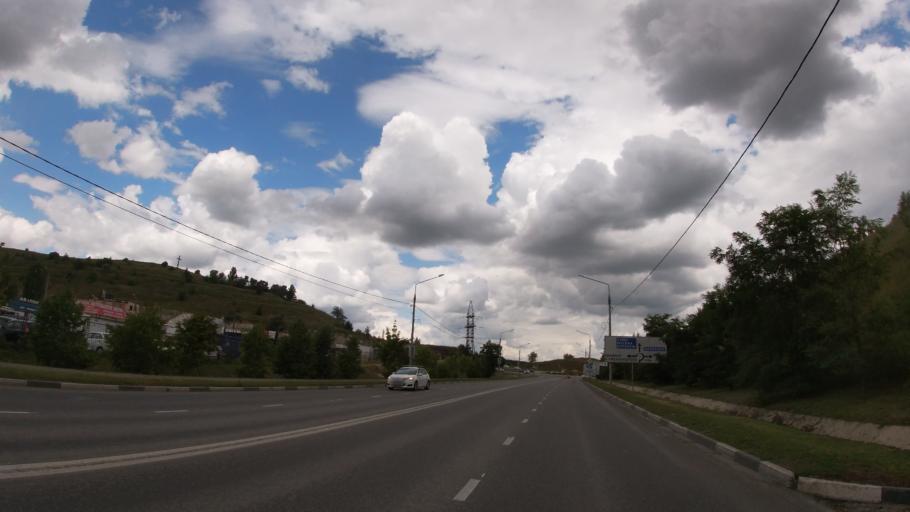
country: RU
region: Belgorod
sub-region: Belgorodskiy Rayon
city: Belgorod
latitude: 50.6158
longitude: 36.6147
